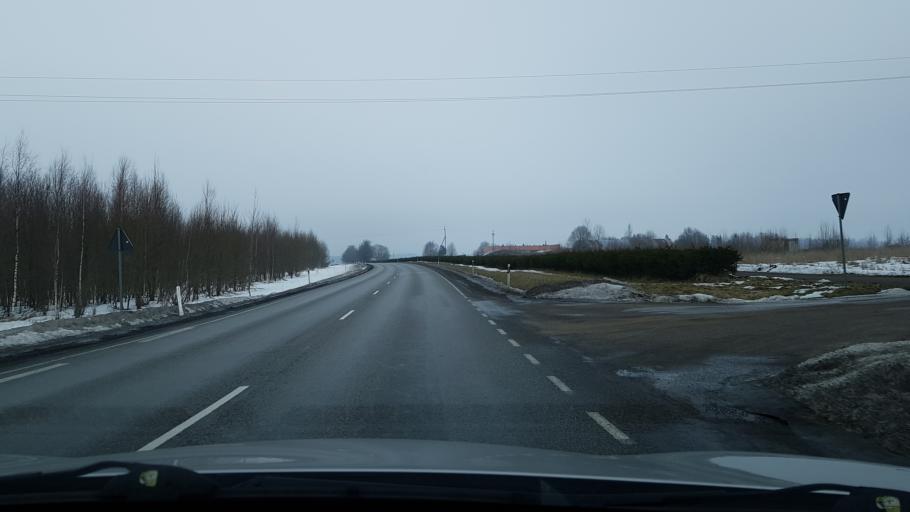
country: EE
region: Valgamaa
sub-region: Valga linn
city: Valga
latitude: 57.9276
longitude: 26.1752
